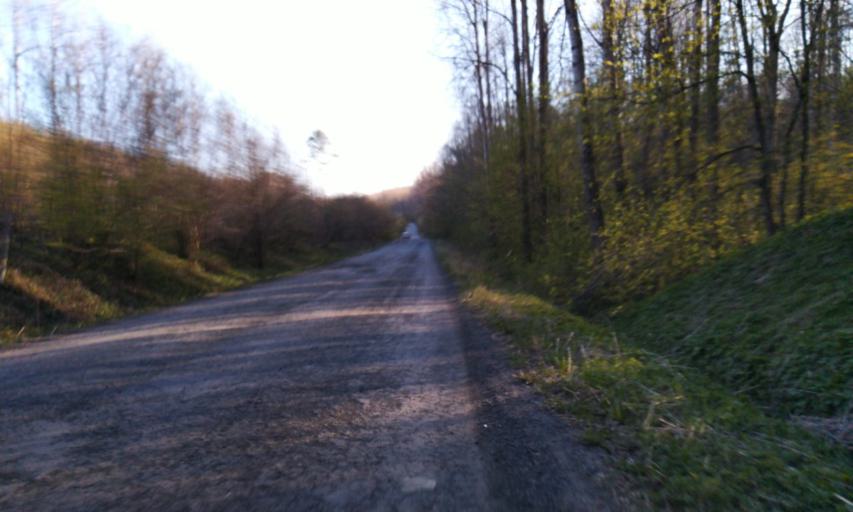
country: RU
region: Leningrad
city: Toksovo
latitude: 60.1453
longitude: 30.5759
